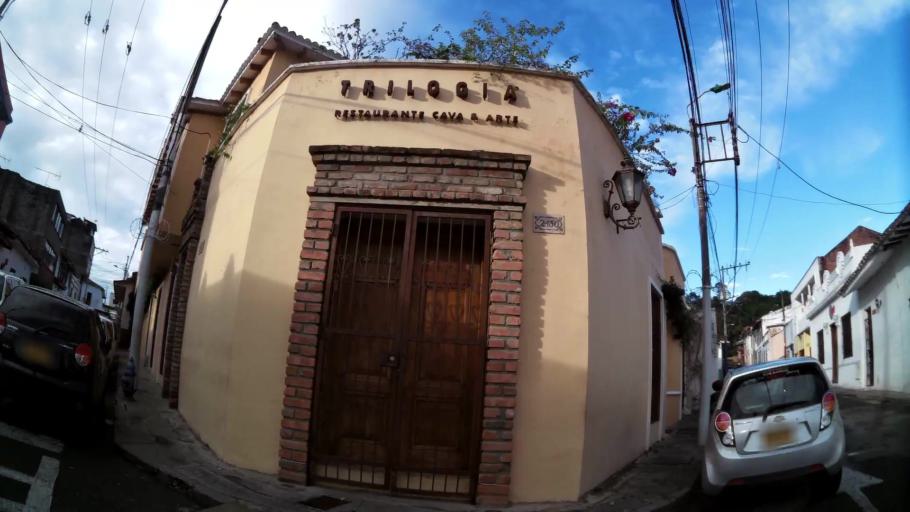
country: CO
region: Valle del Cauca
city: Cali
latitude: 3.4477
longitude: -76.5389
